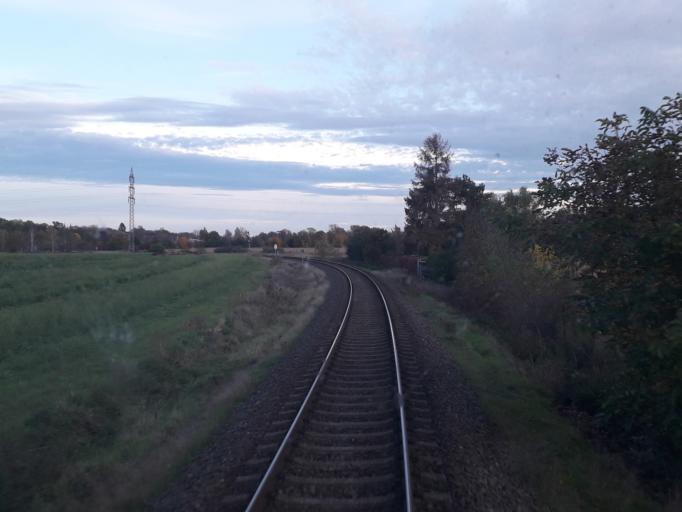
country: DE
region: Brandenburg
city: Neuruppin
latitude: 52.9238
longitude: 12.7845
